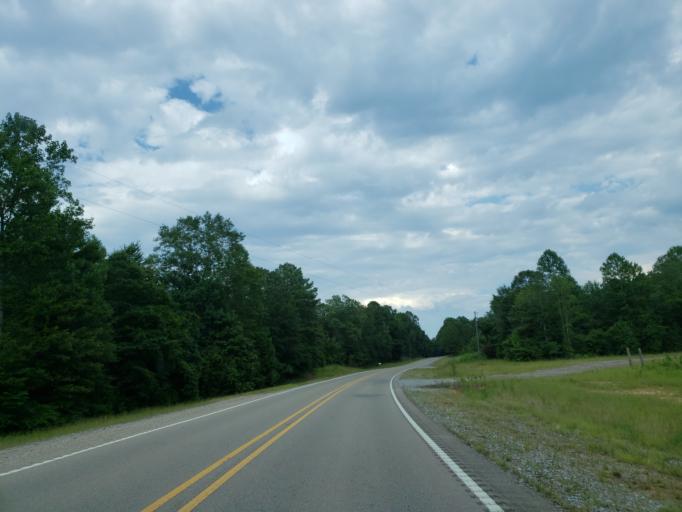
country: US
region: Mississippi
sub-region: Clarke County
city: Stonewall
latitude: 32.1784
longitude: -88.9232
